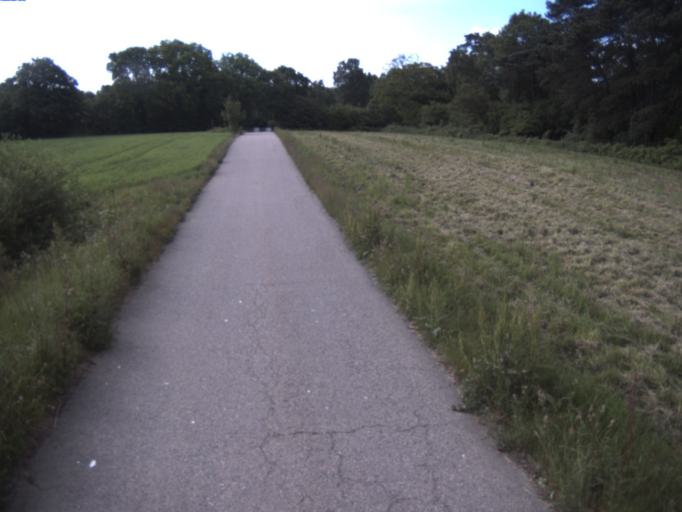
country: SE
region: Skane
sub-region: Helsingborg
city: Helsingborg
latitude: 56.0748
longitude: 12.6695
